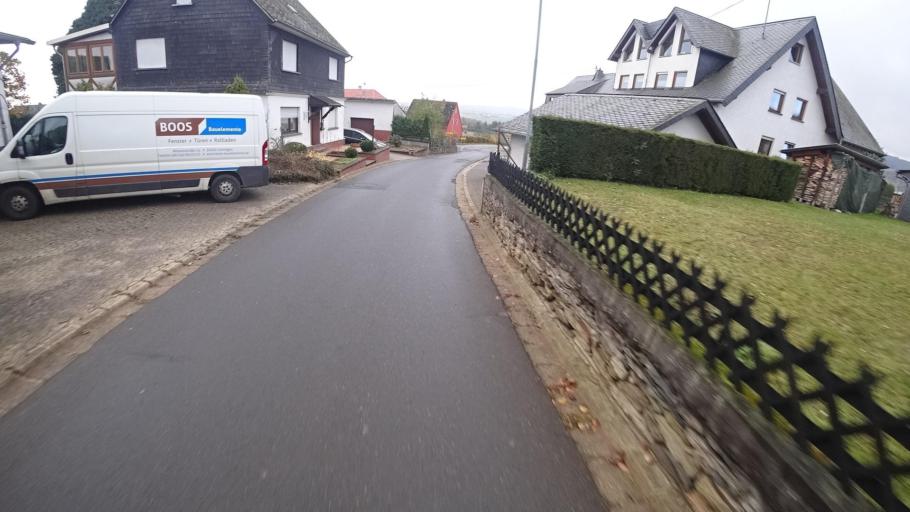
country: DE
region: Rheinland-Pfalz
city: Niederburg
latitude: 50.1177
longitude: 7.6926
